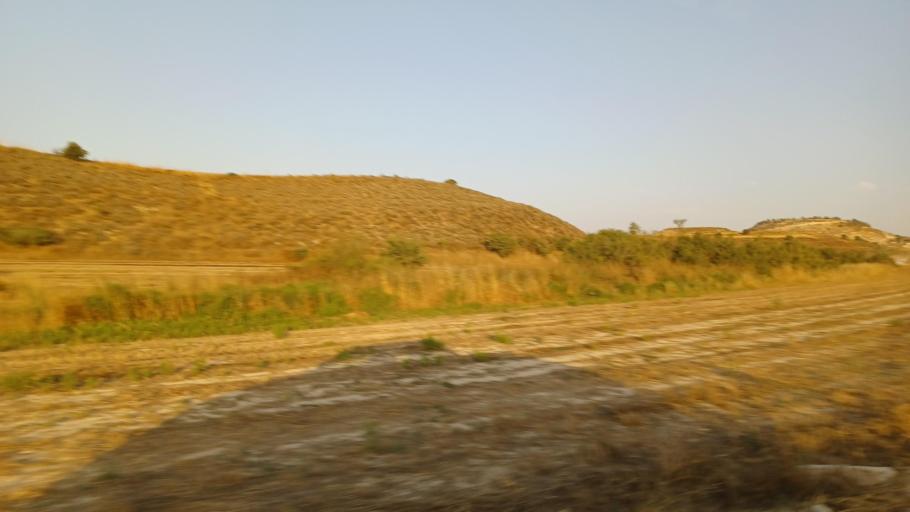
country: CY
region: Lefkosia
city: Lympia
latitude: 34.9966
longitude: 33.5205
